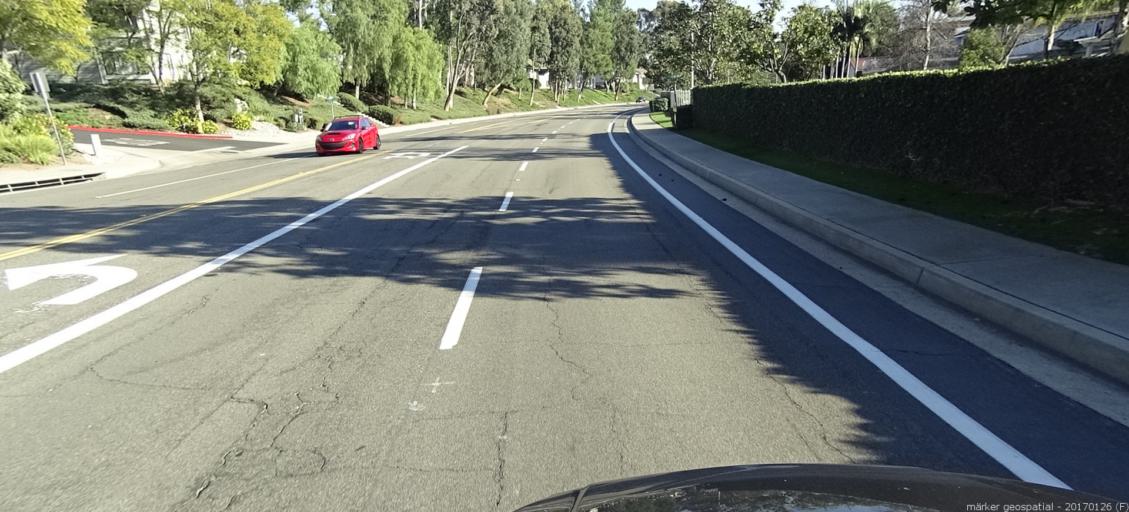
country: US
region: California
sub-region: Orange County
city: Lake Forest
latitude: 33.6489
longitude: -117.7047
